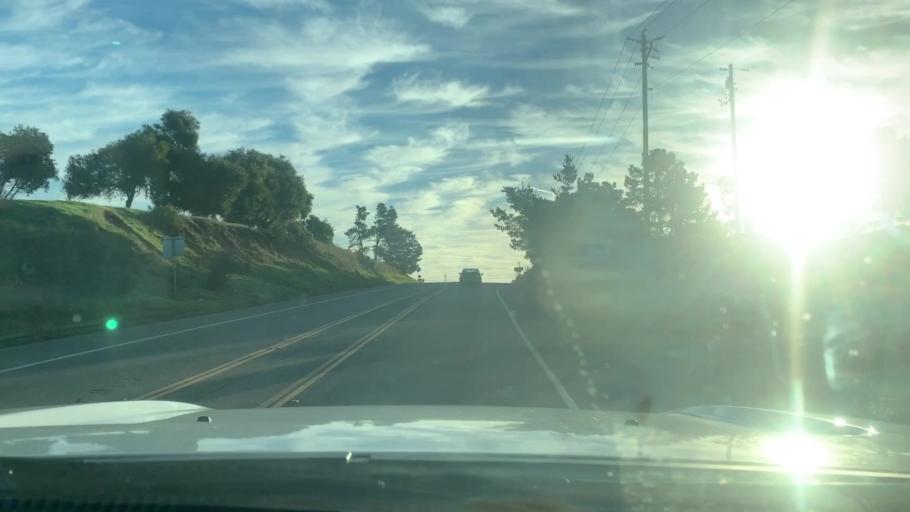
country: US
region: California
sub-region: San Luis Obispo County
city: Los Osos
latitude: 35.3044
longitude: -120.8051
